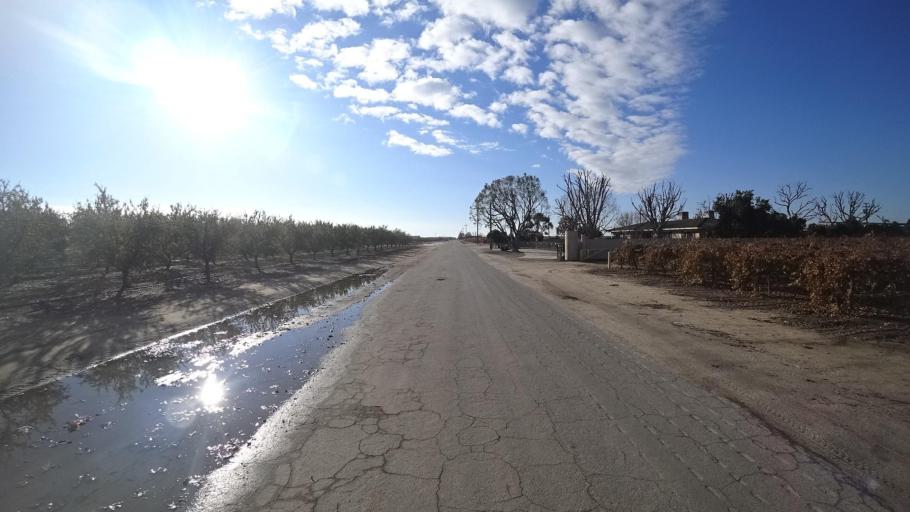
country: US
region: California
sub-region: Kern County
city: McFarland
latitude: 35.7077
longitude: -119.3030
